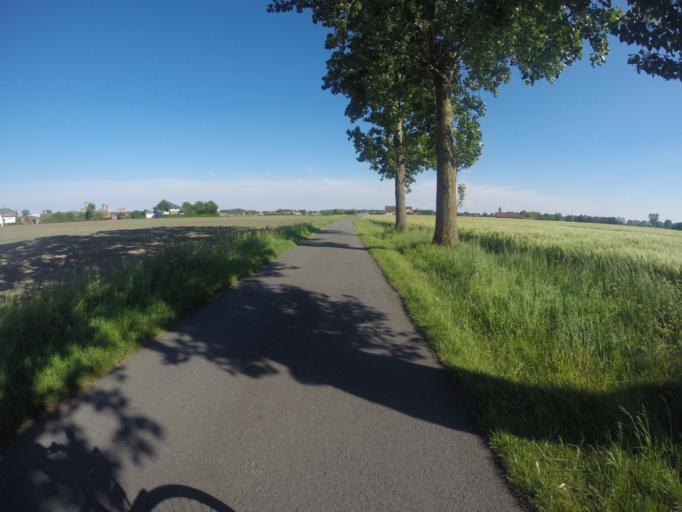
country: BE
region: Flanders
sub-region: Provincie Oost-Vlaanderen
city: Aalter
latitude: 51.0628
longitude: 3.4346
